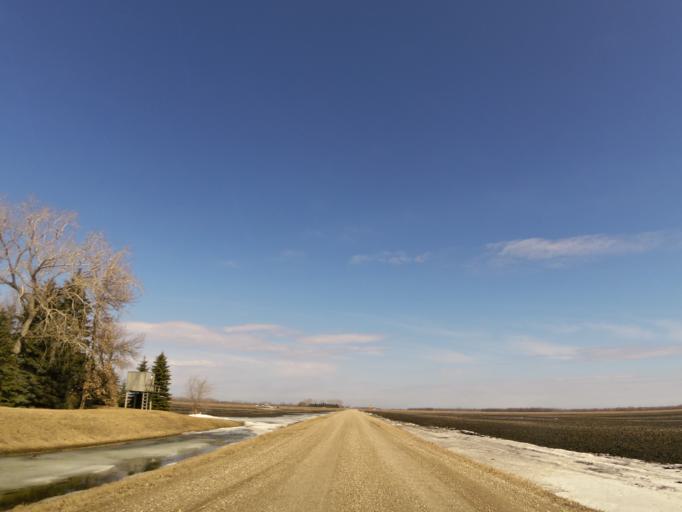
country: US
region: North Dakota
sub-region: Walsh County
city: Grafton
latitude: 48.4076
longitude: -97.1686
